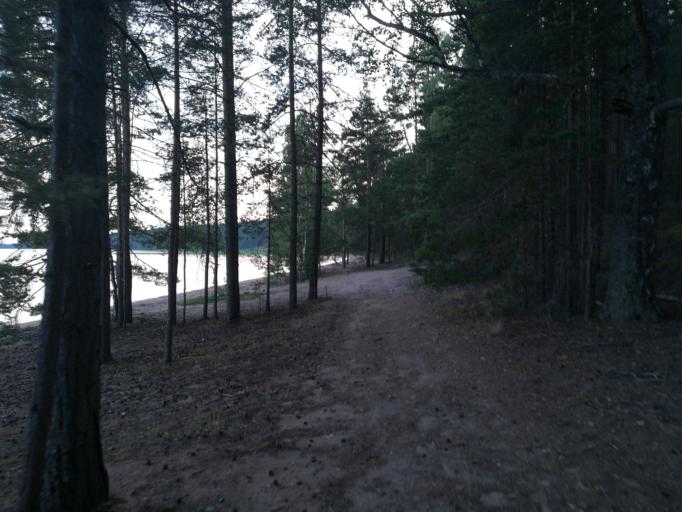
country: FI
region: South Karelia
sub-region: Lappeenranta
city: Joutseno
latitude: 61.3360
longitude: 28.3969
